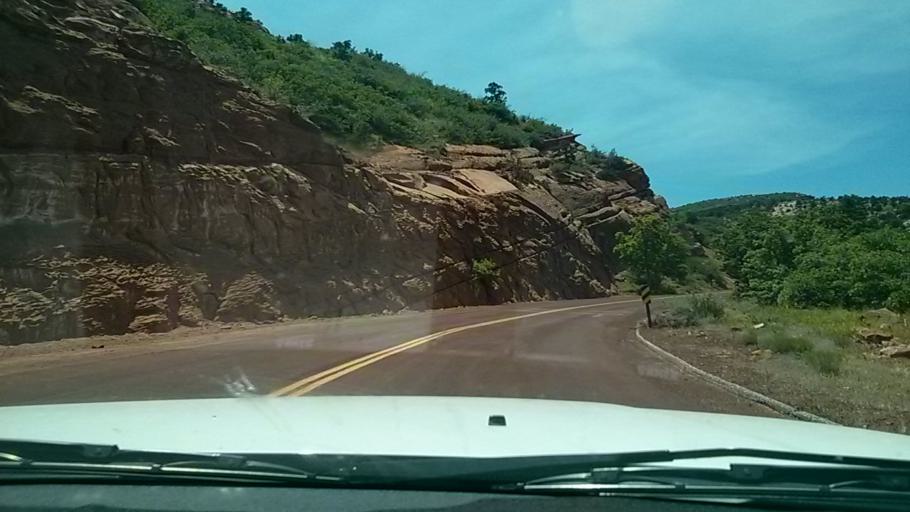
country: US
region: Utah
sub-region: Washington County
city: Toquerville
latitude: 37.4549
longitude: -113.1843
